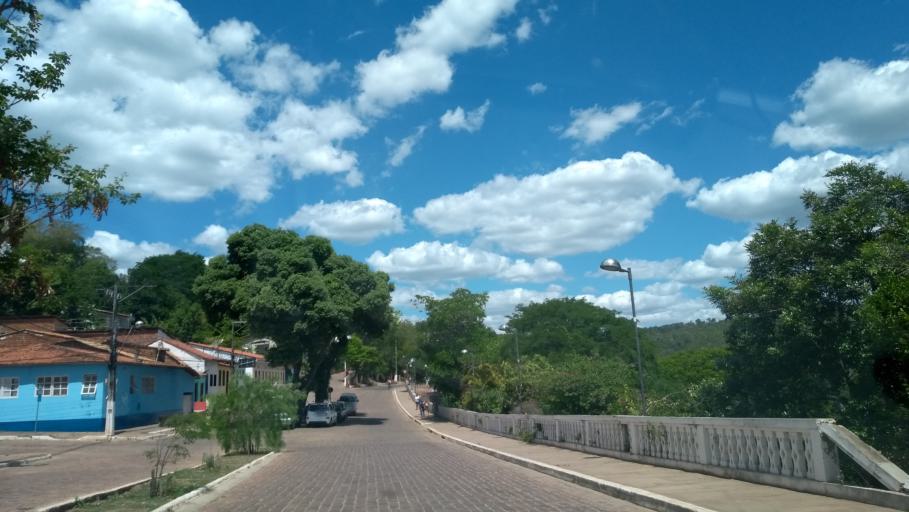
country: BR
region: Bahia
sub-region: Andarai
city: Vera Cruz
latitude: -12.5614
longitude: -41.3887
